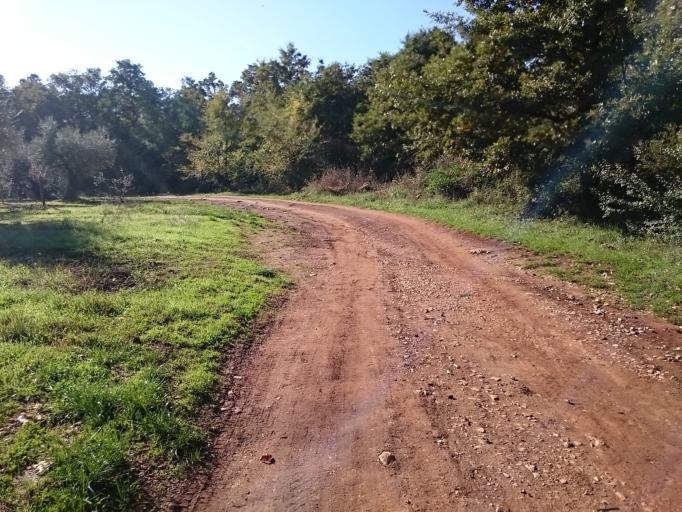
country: HR
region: Istarska
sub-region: Grad Porec
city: Porec
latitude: 45.2684
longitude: 13.5808
